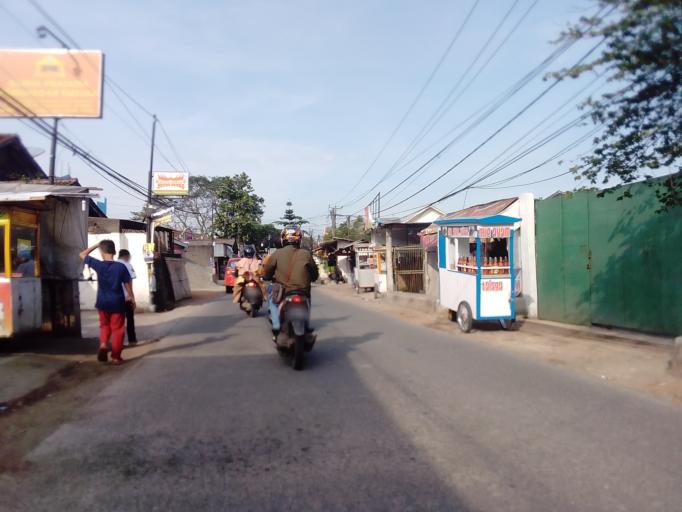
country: ID
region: West Java
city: Cileunyi
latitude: -6.9239
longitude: 107.6997
